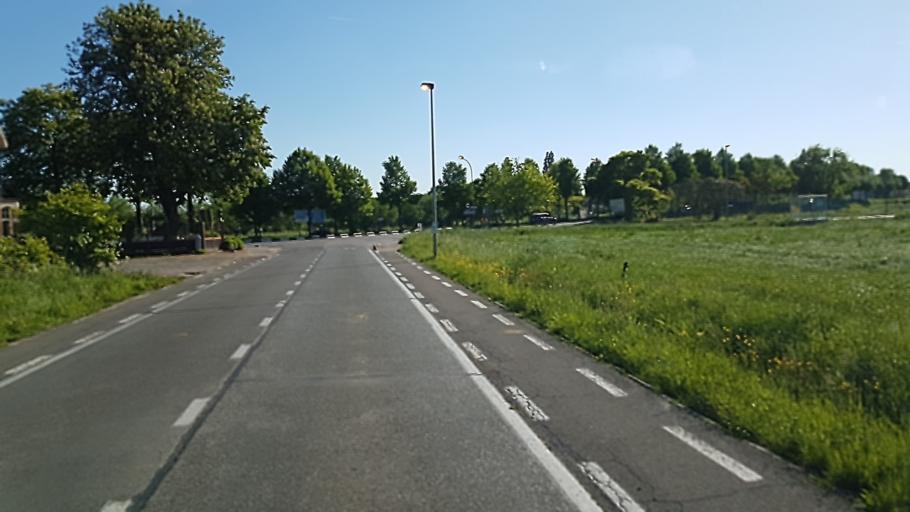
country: BE
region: Flanders
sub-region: Provincie Antwerpen
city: Heist-op-den-Berg
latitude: 51.1018
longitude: 4.7399
